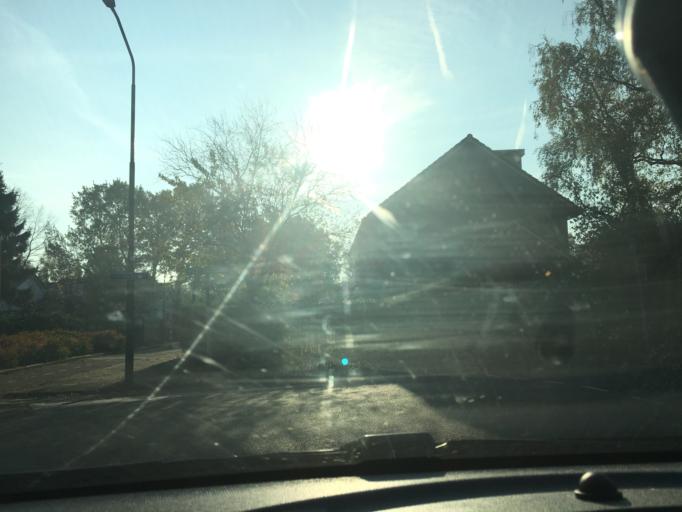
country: NL
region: North Brabant
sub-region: Gemeente Waalre
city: Waalre
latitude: 51.3944
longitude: 5.4694
